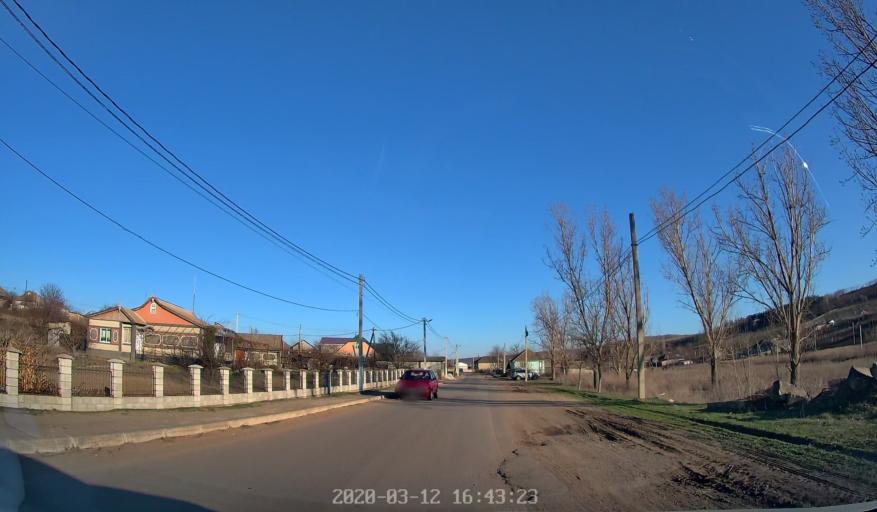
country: MD
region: Anenii Noi
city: Anenii Noi
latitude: 46.8202
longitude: 29.1409
